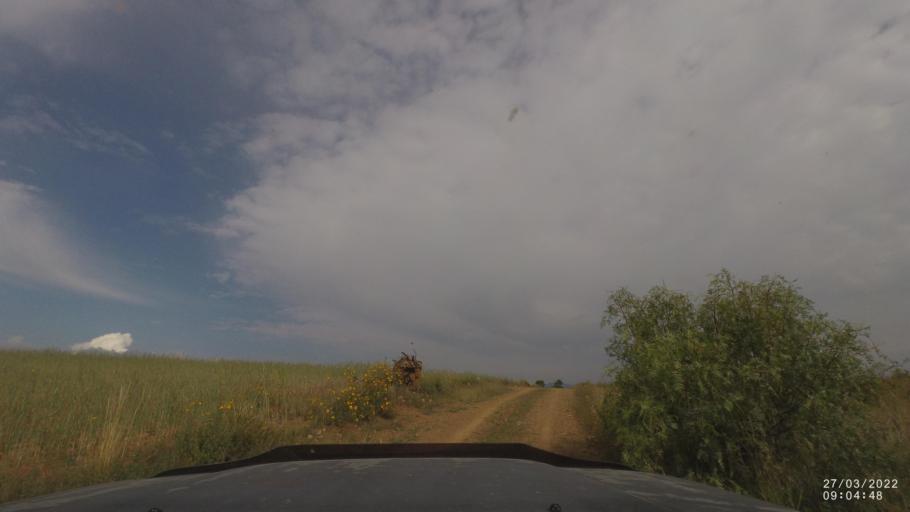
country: BO
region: Cochabamba
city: Cliza
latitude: -17.7333
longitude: -65.8659
